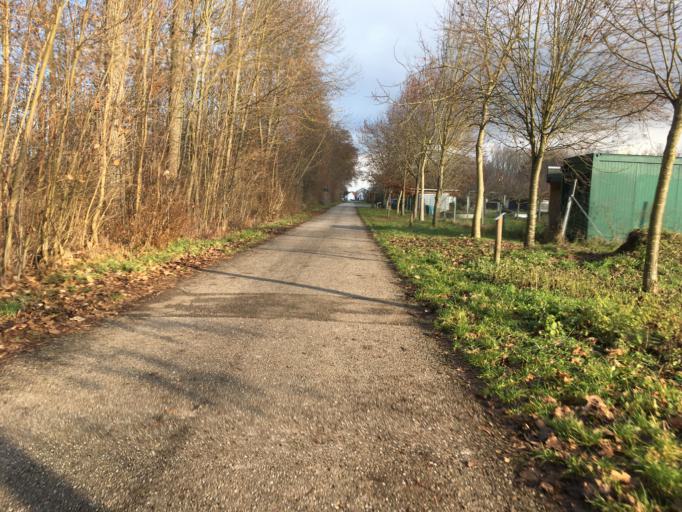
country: DE
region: Rheinland-Pfalz
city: Germersheim
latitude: 49.2298
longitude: 8.3987
